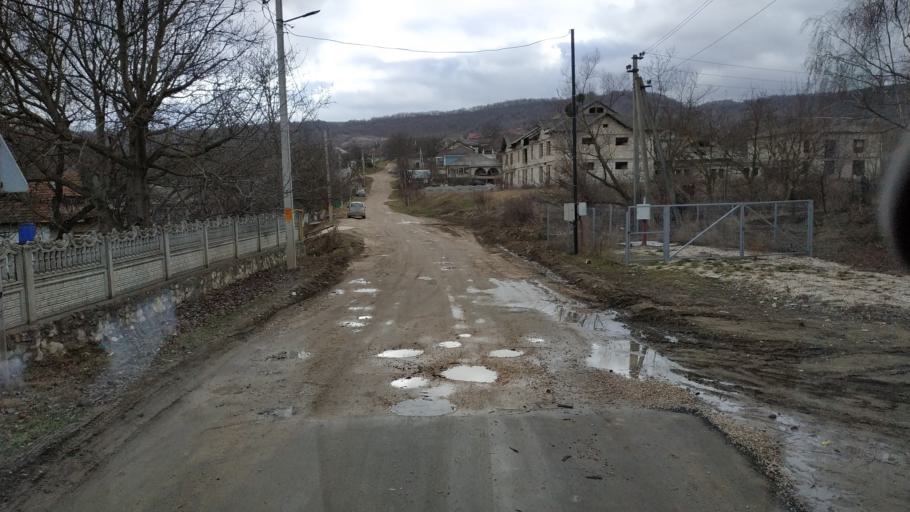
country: MD
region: Calarasi
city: Calarasi
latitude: 47.2384
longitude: 28.3104
